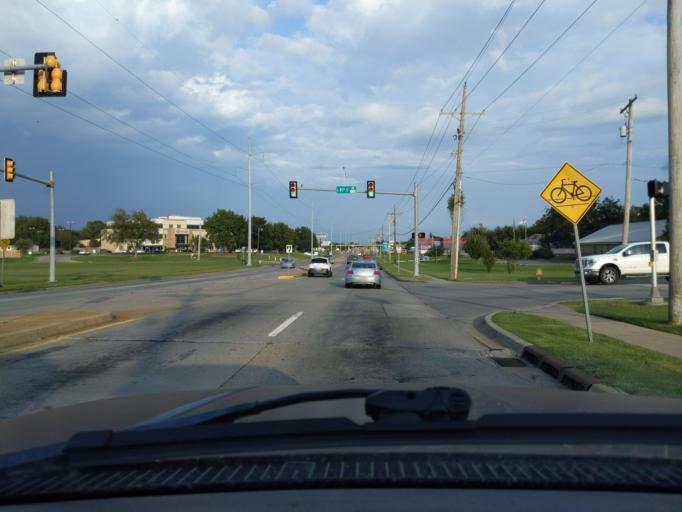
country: US
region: Oklahoma
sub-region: Tulsa County
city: Broken Arrow
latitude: 36.1334
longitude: -95.8758
